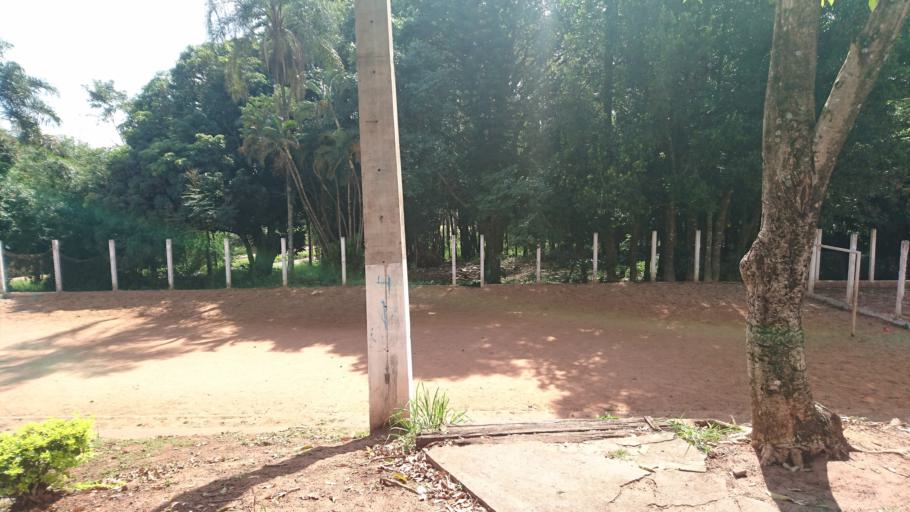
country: BR
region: Sao Paulo
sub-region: Casa Branca
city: Casa Branca
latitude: -21.7828
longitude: -47.0892
